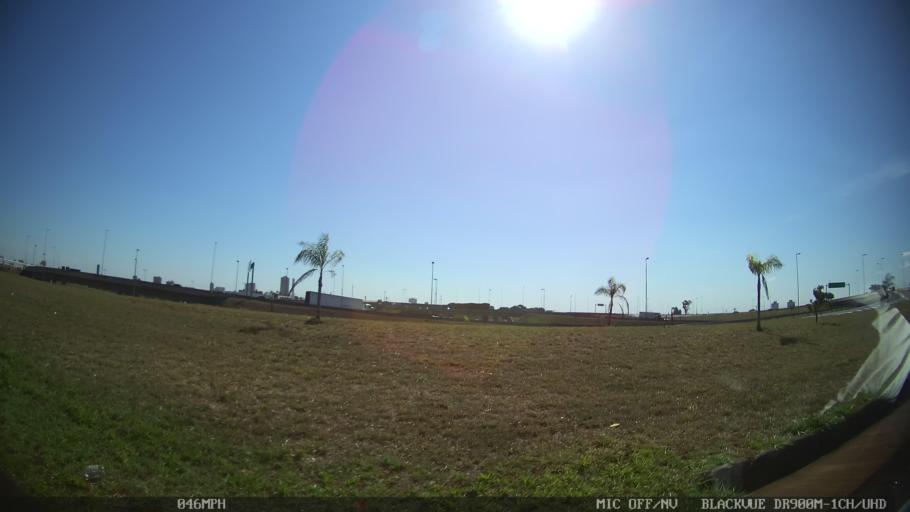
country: BR
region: Sao Paulo
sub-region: Ribeirao Preto
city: Ribeirao Preto
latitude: -21.2077
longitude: -47.7571
